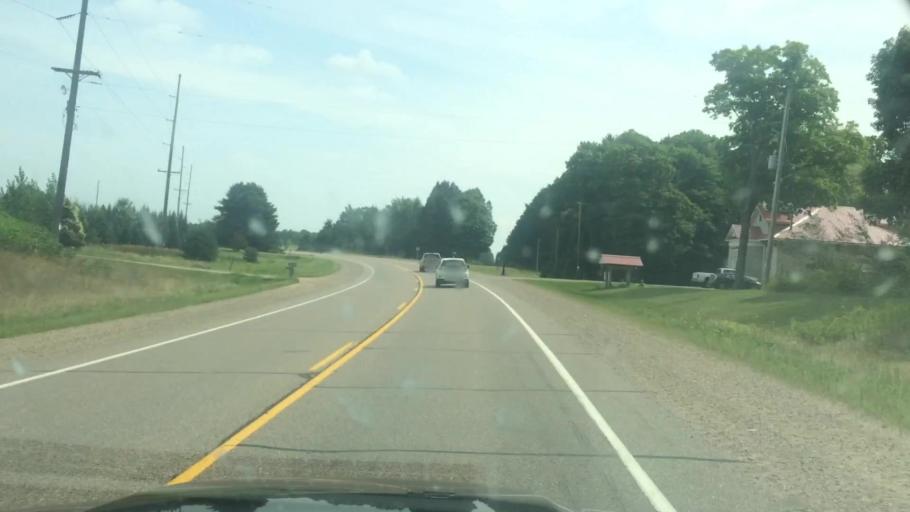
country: US
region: Wisconsin
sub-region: Langlade County
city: Antigo
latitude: 45.1613
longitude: -89.0199
